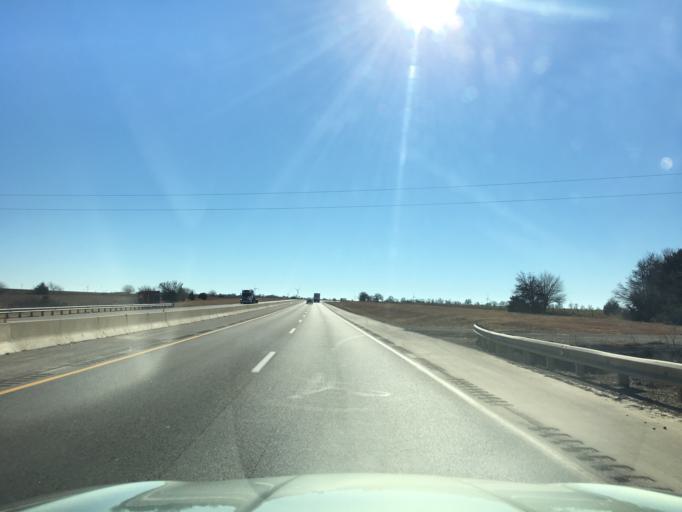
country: US
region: Kansas
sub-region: Sumner County
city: Wellington
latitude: 37.1892
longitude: -97.3416
